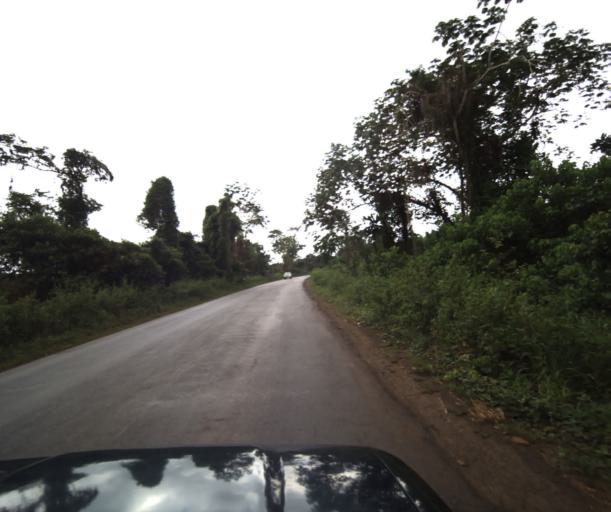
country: CM
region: Centre
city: Eseka
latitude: 3.8901
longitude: 10.7365
